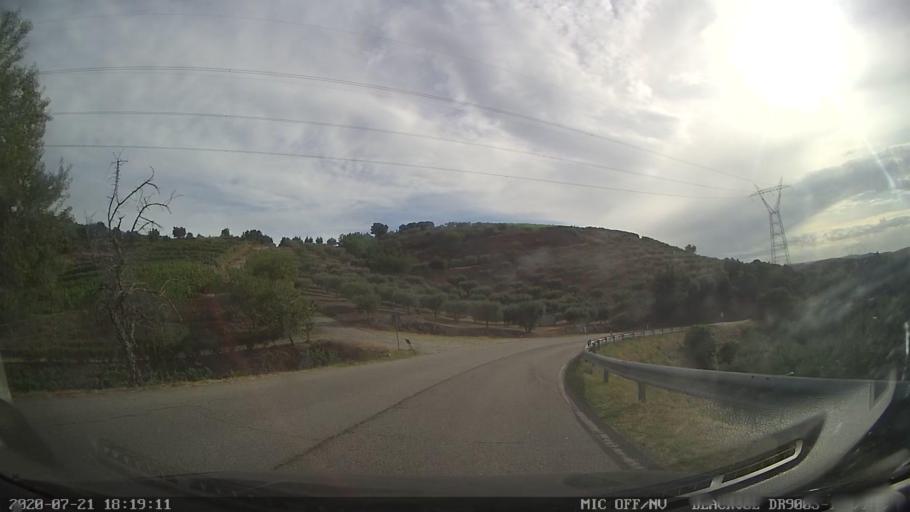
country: PT
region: Guarda
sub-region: Vila Nova de Foz Coa
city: Custoias
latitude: 41.0934
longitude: -7.3712
